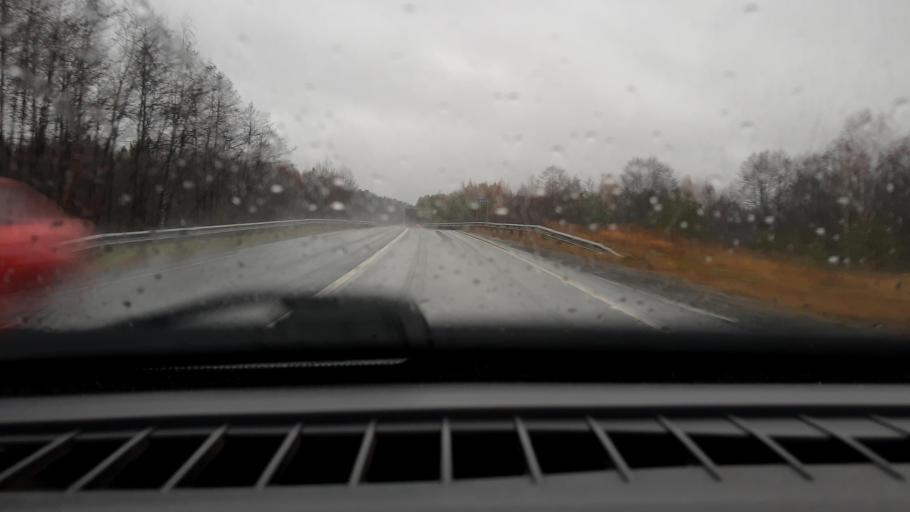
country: RU
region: Nizjnij Novgorod
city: Linda
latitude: 56.6601
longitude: 44.1274
